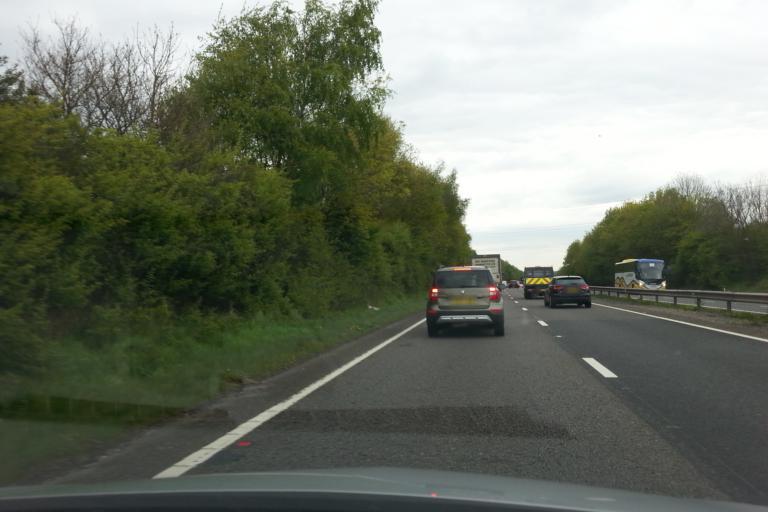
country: GB
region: England
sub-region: Derbyshire
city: Melbourne
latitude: 52.7880
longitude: -1.4094
